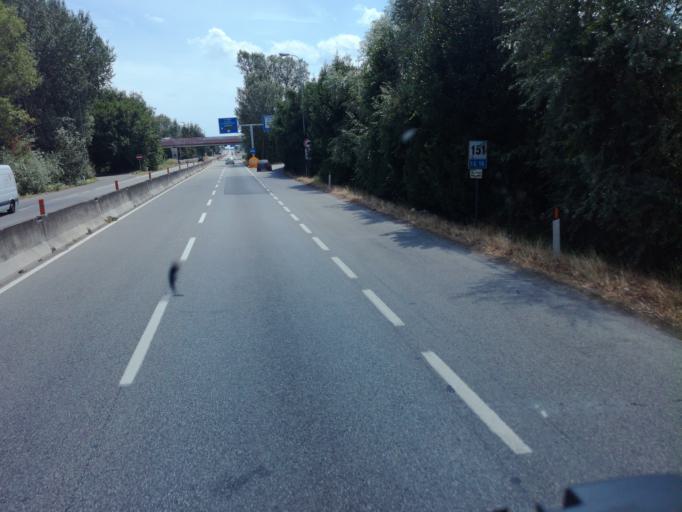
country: IT
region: Emilia-Romagna
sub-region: Provincia di Ravenna
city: Ravenna
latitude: 44.4012
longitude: 12.1793
